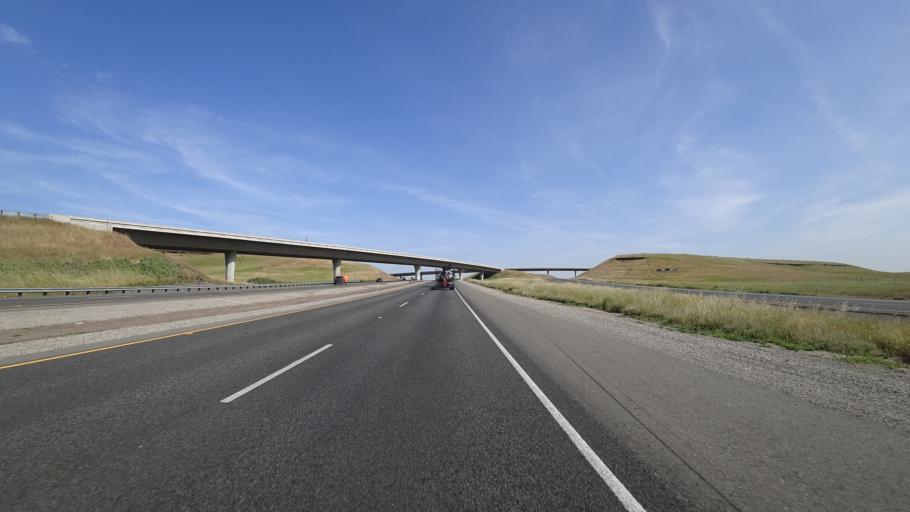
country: US
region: California
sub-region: Butte County
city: Durham
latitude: 39.6236
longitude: -121.6951
